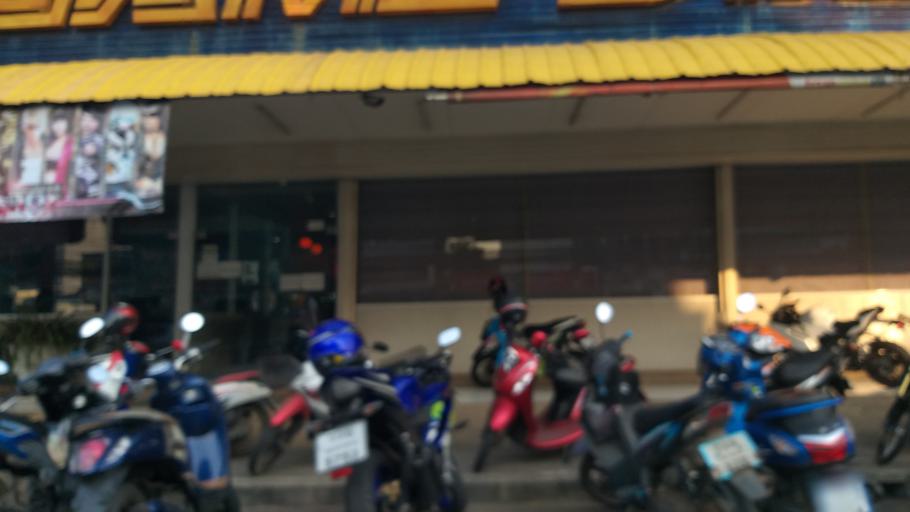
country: TH
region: Khon Kaen
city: Khon Kaen
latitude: 16.4185
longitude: 102.8327
